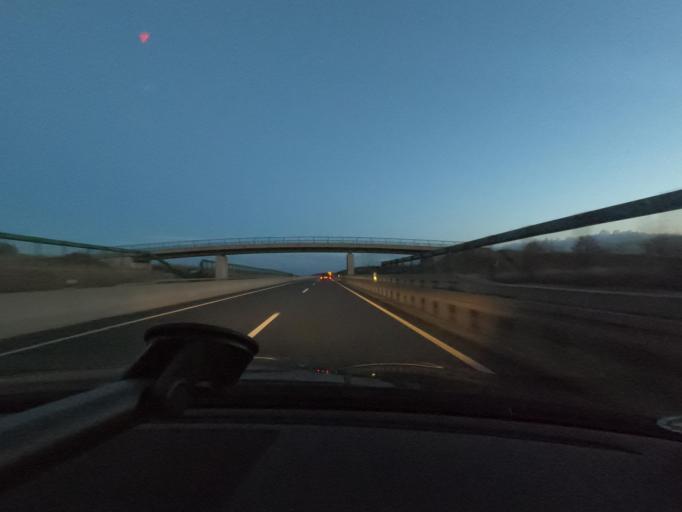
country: DE
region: Lower Saxony
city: Bad Lauterberg im Harz
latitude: 51.5902
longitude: 10.4991
